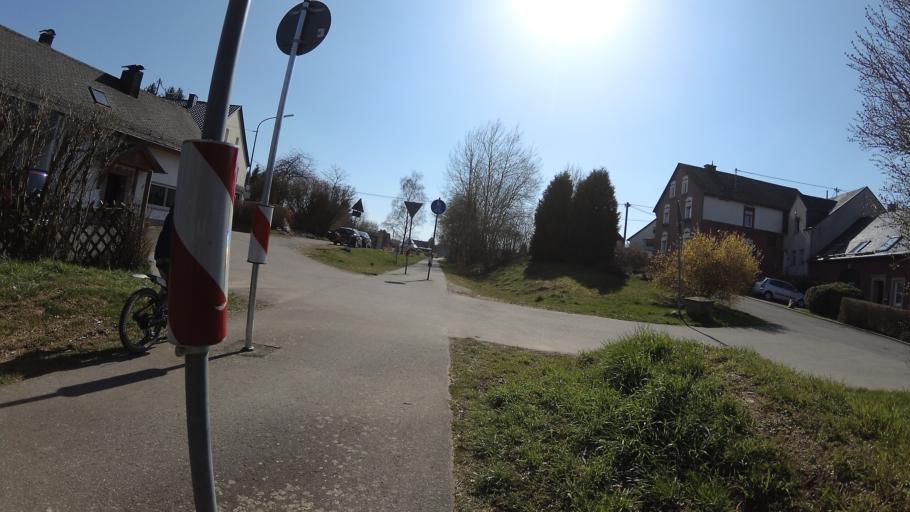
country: DE
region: Rheinland-Pfalz
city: Reinsfeld
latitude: 49.6773
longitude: 6.8791
